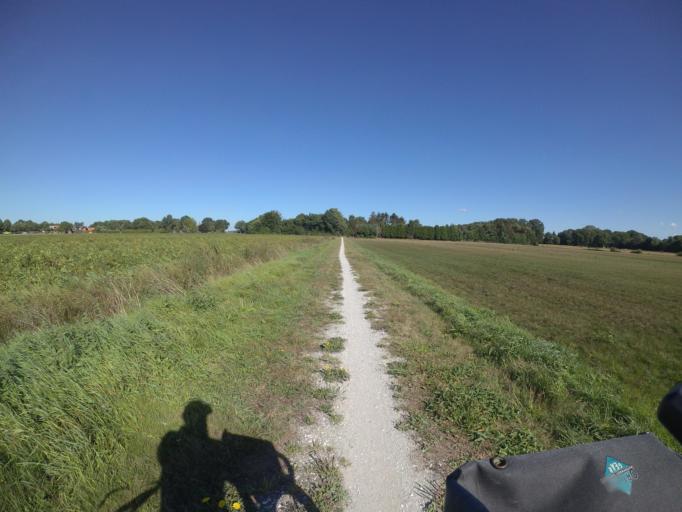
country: NL
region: Drenthe
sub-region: Gemeente Hoogeveen
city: Hoogeveen
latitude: 52.7237
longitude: 6.6119
